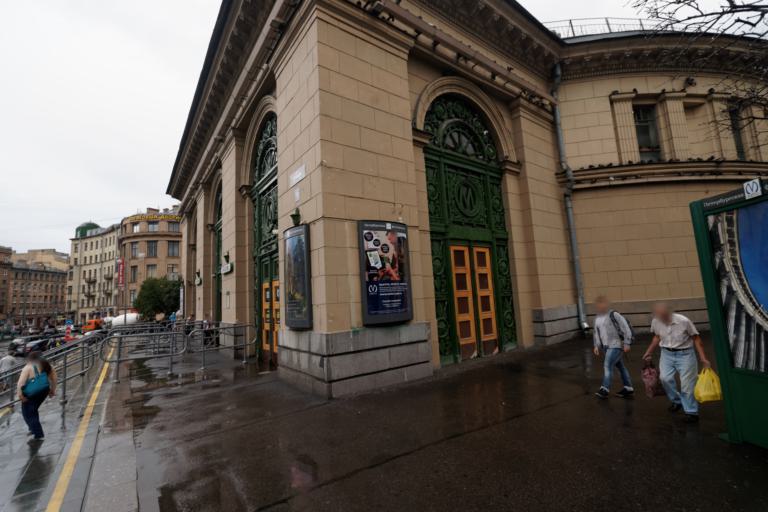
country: RU
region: St.-Petersburg
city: Admiralteisky
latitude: 59.9009
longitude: 30.2746
